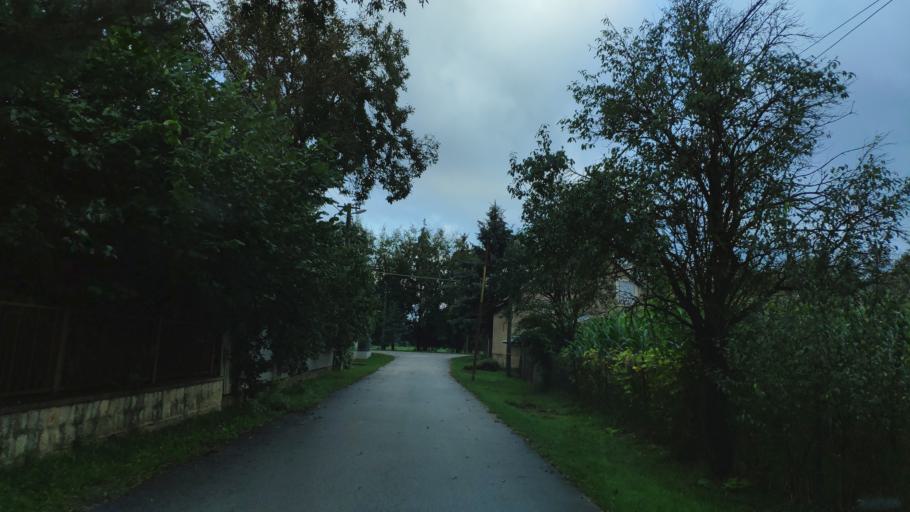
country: SK
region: Kosicky
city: Moldava nad Bodvou
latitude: 48.5764
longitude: 20.9551
